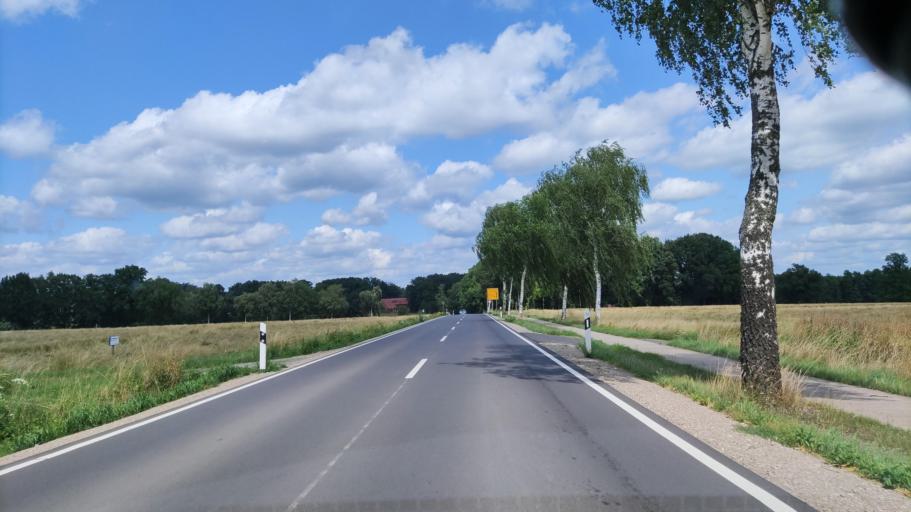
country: DE
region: Lower Saxony
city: Bomlitz
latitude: 52.8959
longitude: 9.6118
